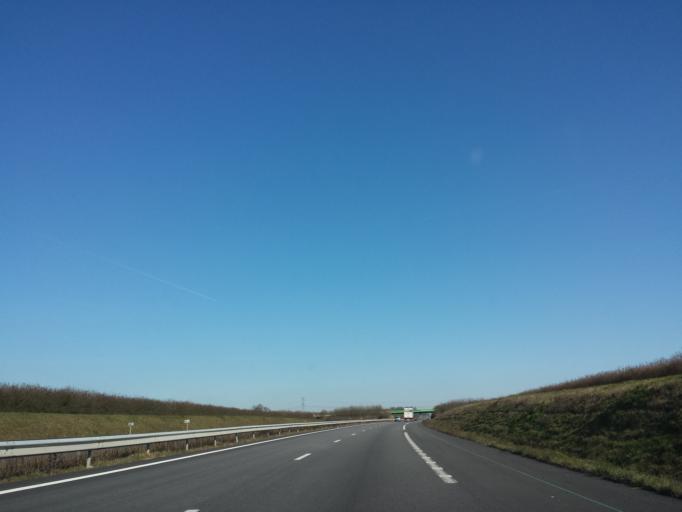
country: FR
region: Picardie
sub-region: Departement de l'Oise
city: Saint-Crepin-Ibouvillers
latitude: 49.2989
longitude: 2.0728
